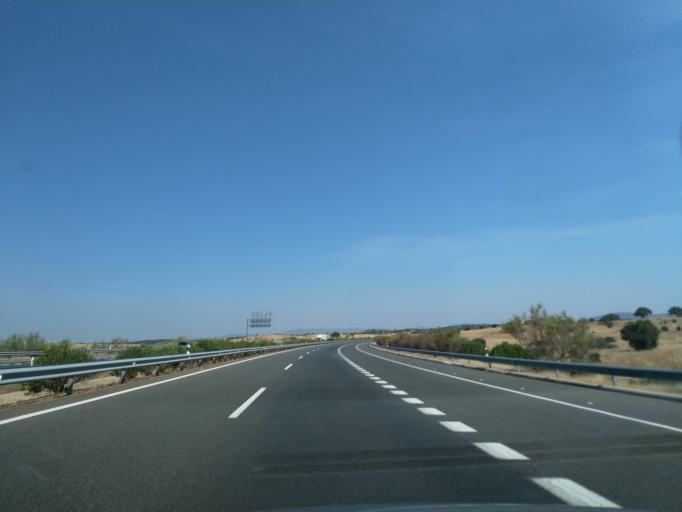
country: ES
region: Extremadura
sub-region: Provincia de Badajoz
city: Mirandilla
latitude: 38.9801
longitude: -6.3340
